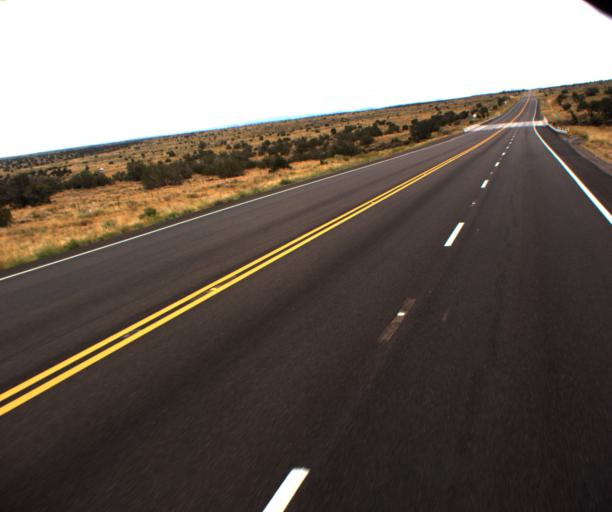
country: US
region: Arizona
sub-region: Navajo County
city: Snowflake
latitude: 34.5935
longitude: -110.0869
